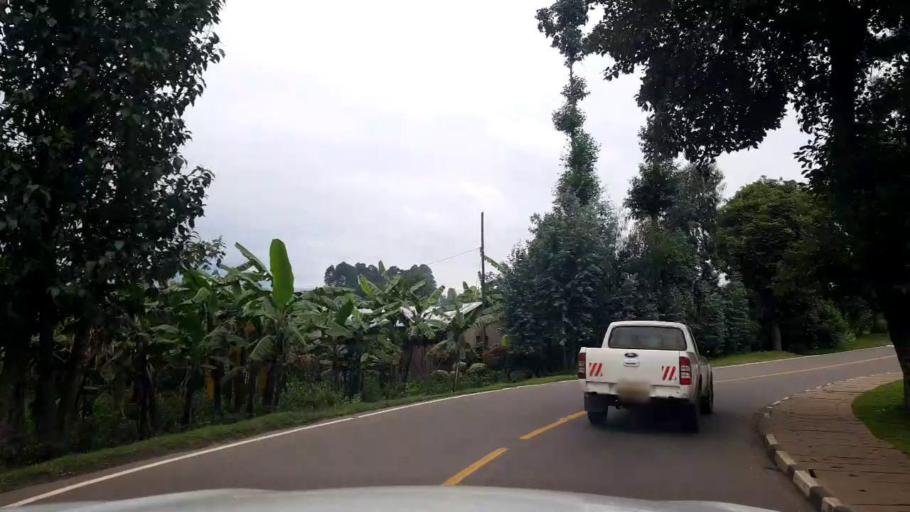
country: RW
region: Northern Province
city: Musanze
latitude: -1.4653
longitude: 29.6154
